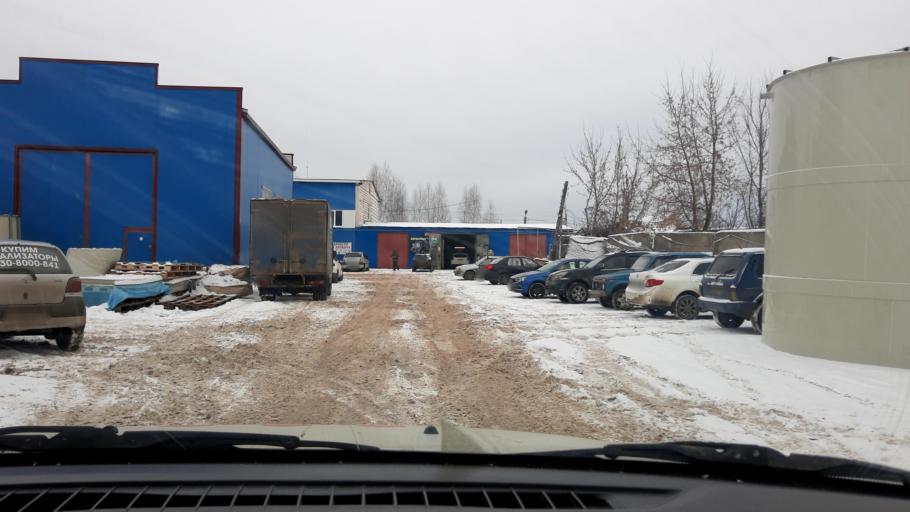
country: RU
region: Nizjnij Novgorod
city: Gorodets
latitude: 56.6578
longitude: 43.4843
